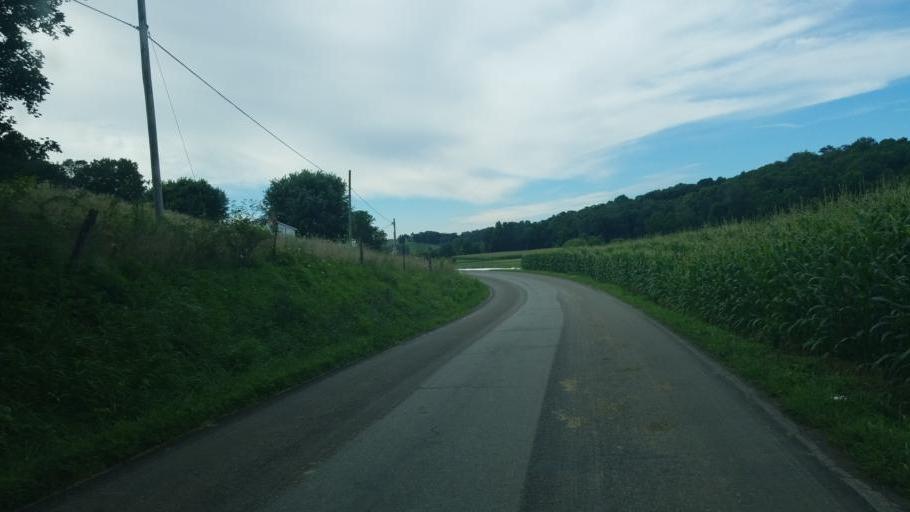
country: US
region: Ohio
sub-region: Holmes County
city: Millersburg
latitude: 40.4803
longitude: -81.8567
